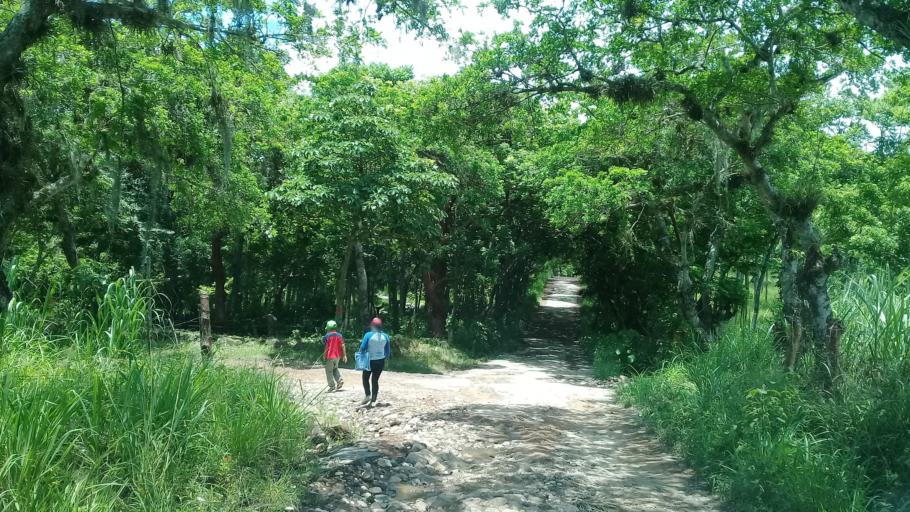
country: MX
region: Veracruz
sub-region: Naolinco
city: El Espinal
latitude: 19.5918
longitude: -96.8745
